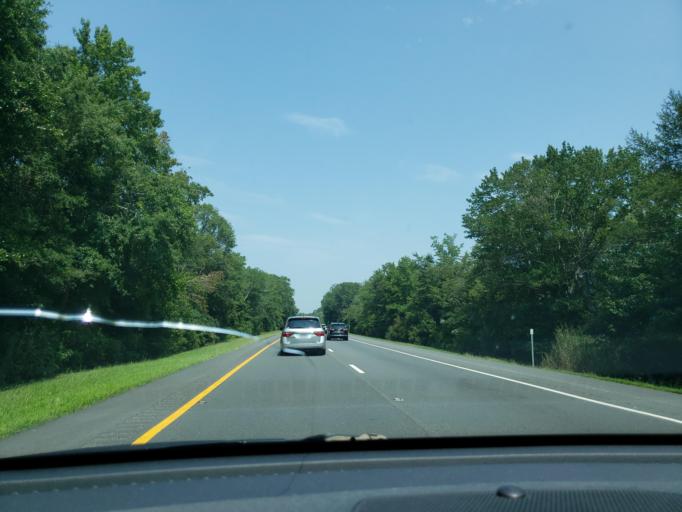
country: US
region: New Jersey
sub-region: Cape May County
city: Avalon
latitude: 39.1329
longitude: -74.7673
